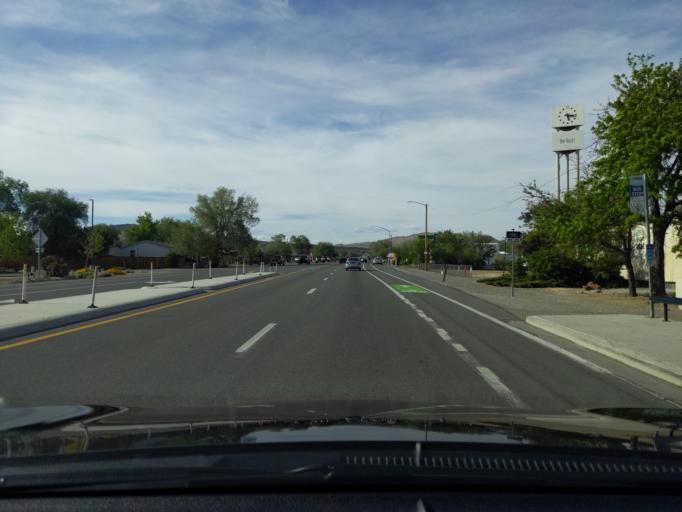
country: US
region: Nevada
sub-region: Washoe County
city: Sun Valley
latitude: 39.5856
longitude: -119.7803
